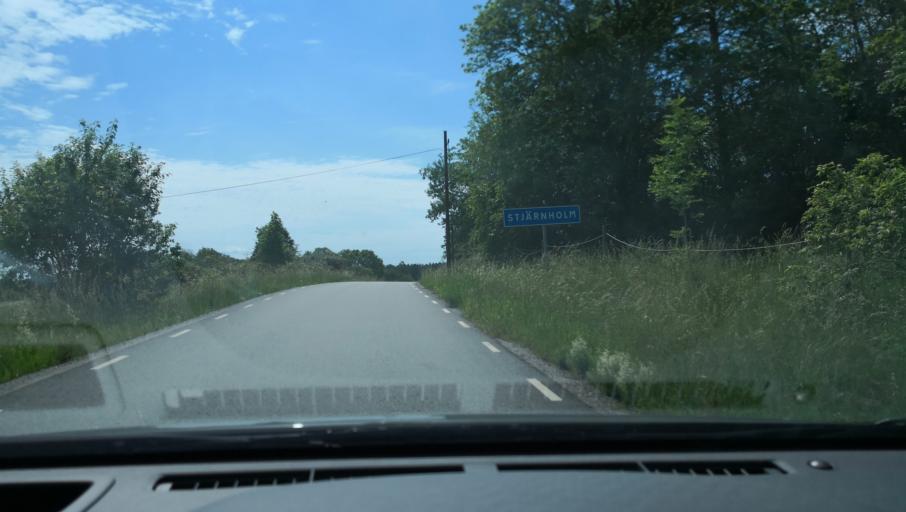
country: SE
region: Uppsala
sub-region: Habo Kommun
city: Balsta
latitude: 59.6880
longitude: 17.4649
